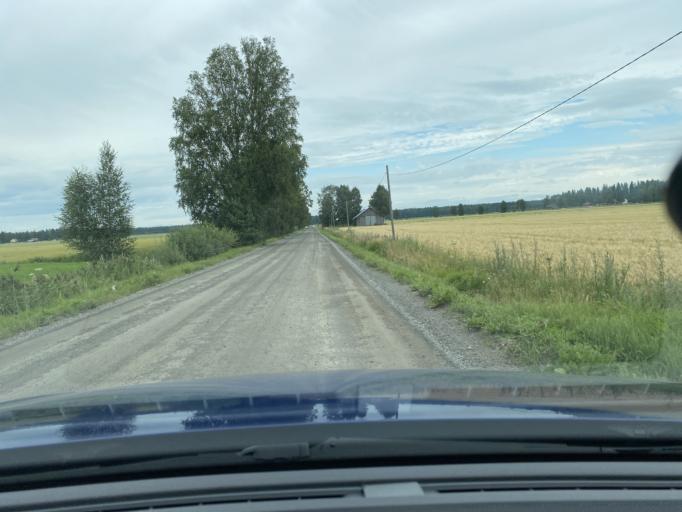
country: FI
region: Satakunta
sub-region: Rauma
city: Kiukainen
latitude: 61.1443
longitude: 21.9982
